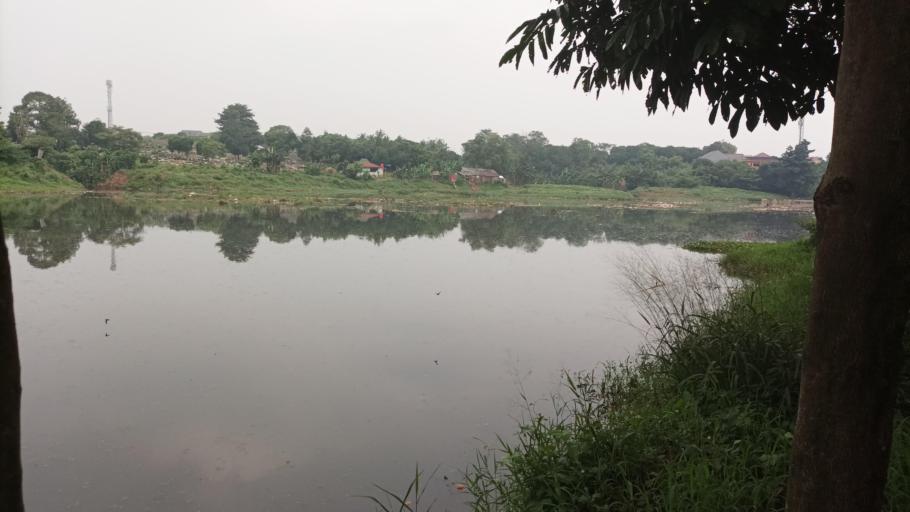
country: ID
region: West Java
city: Depok
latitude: -6.3835
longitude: 106.8592
